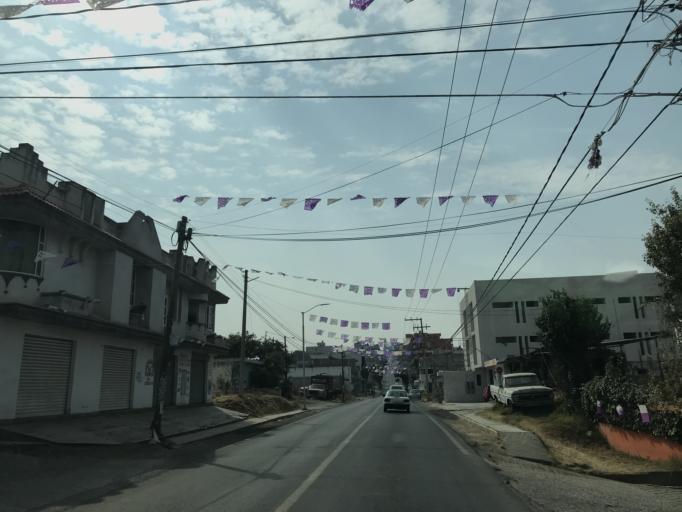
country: MX
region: Tlaxcala
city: Tenancingo
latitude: 19.1505
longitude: -98.2058
